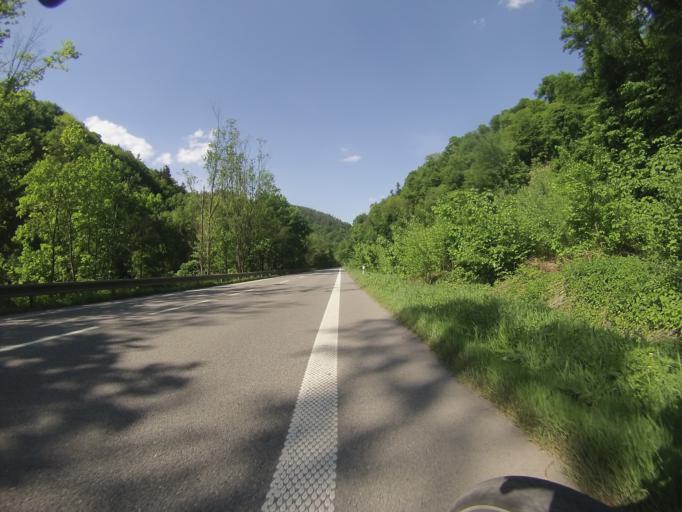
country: CZ
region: South Moravian
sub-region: Okres Blansko
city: Adamov
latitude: 49.3300
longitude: 16.6437
